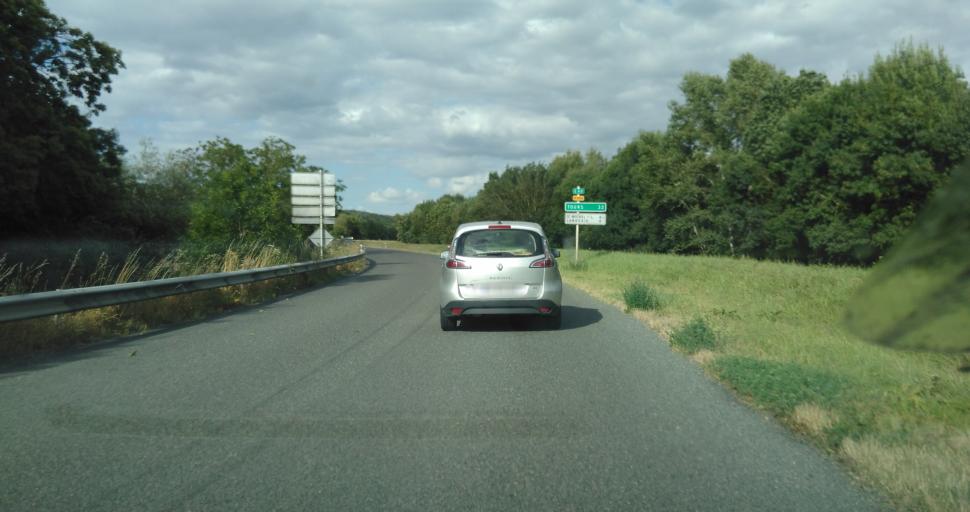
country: FR
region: Centre
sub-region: Departement d'Indre-et-Loire
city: Cheille
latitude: 47.2861
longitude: 0.3260
